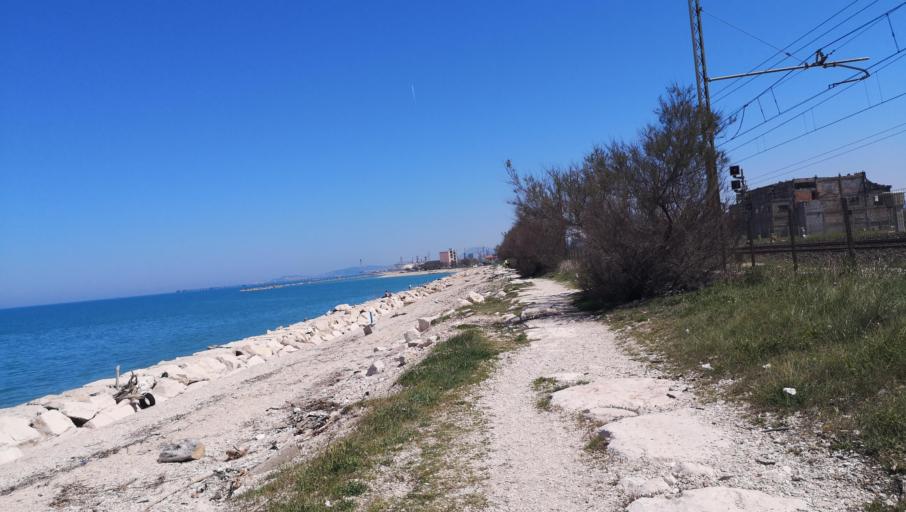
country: IT
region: The Marches
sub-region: Provincia di Ancona
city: Marina di Montemarciano
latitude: 43.6503
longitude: 13.3493
